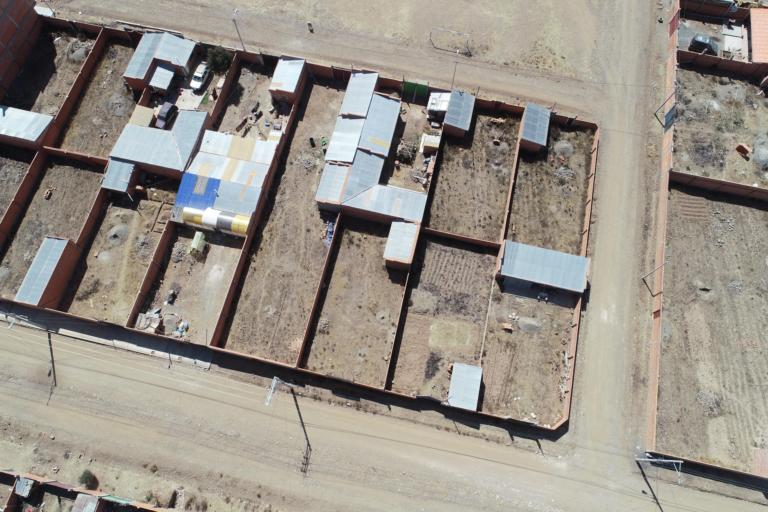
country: BO
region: La Paz
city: La Paz
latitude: -16.5929
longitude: -68.2107
